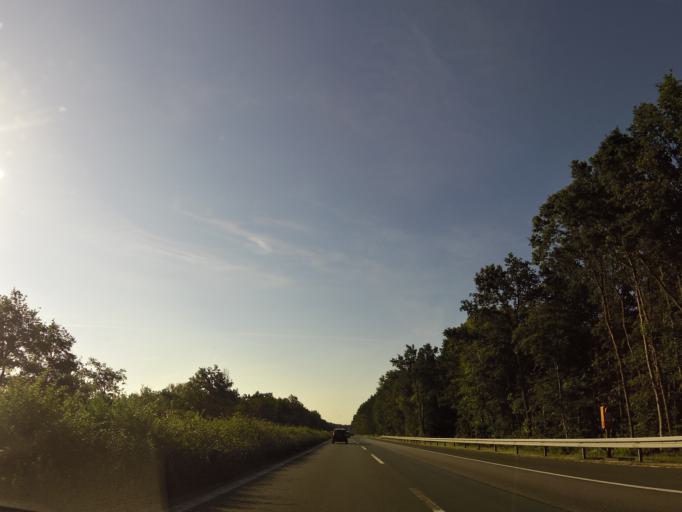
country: DE
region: Bavaria
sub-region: Regierungsbezirk Mittelfranken
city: Grossenseebach
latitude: 49.6692
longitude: 10.8792
